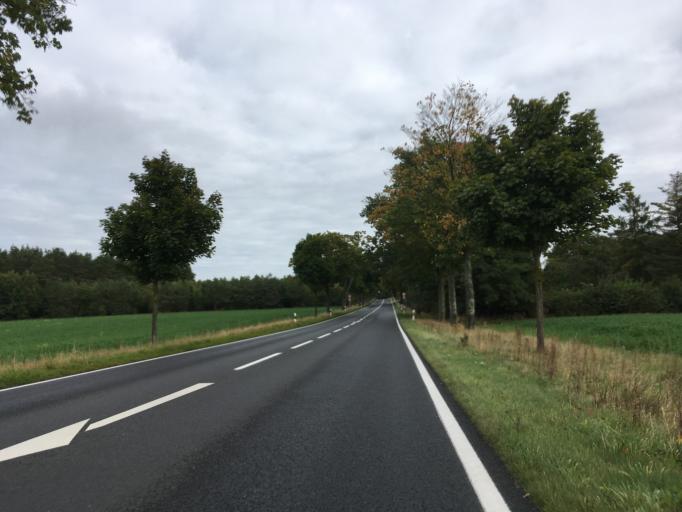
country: DE
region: Brandenburg
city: Werftpfuhl
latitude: 52.6990
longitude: 13.8707
